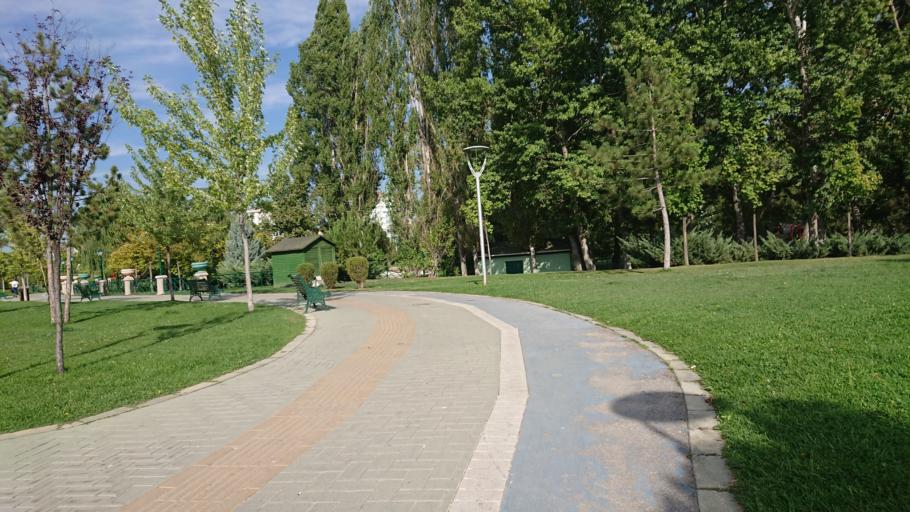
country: TR
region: Eskisehir
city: Eskisehir
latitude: 39.7709
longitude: 30.4983
